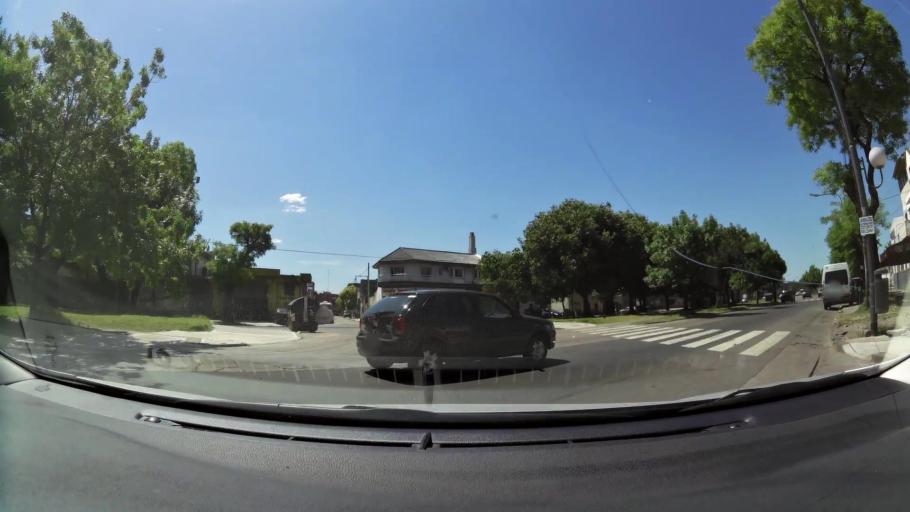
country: AR
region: Buenos Aires
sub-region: Partido de Avellaneda
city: Avellaneda
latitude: -34.6515
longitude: -58.4067
